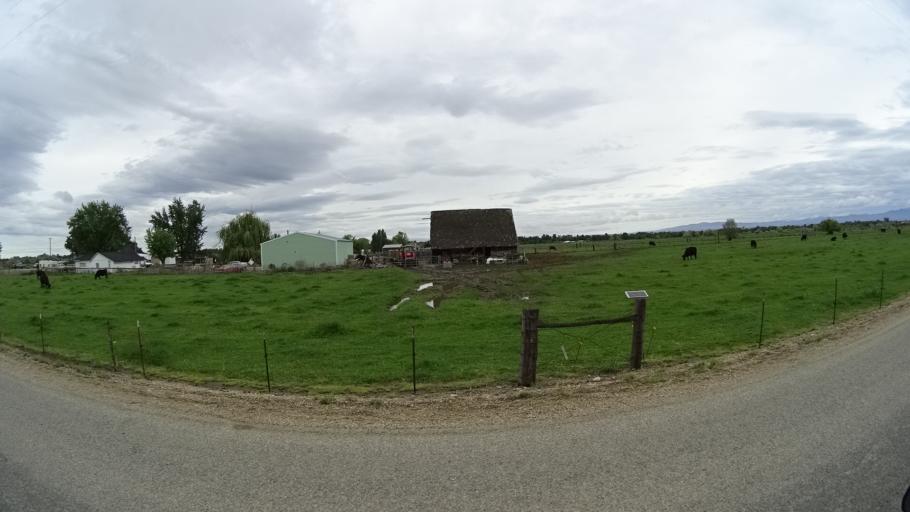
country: US
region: Idaho
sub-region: Ada County
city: Star
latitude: 43.6703
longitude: -116.4918
